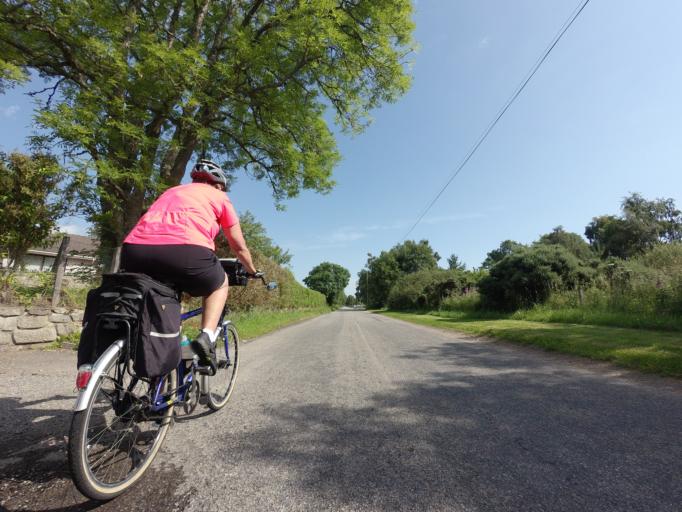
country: GB
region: Scotland
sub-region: Highland
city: Invergordon
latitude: 57.7278
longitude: -4.1950
